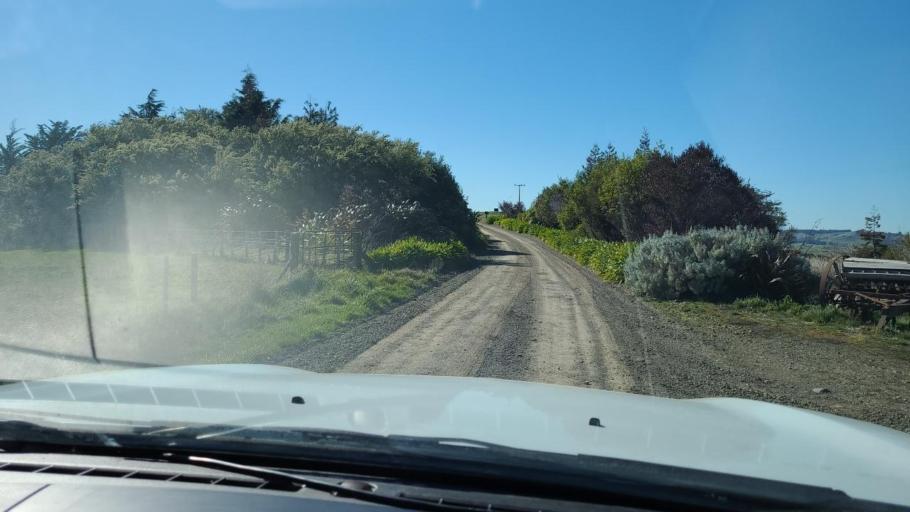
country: NZ
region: Hawke's Bay
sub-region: Napier City
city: Taradale
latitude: -39.4811
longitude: 176.4909
